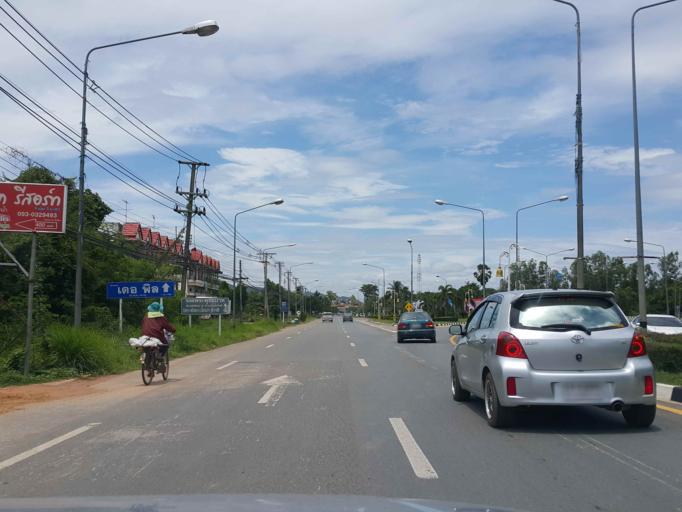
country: TH
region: Sukhothai
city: Ban Na
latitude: 17.0158
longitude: 99.7355
